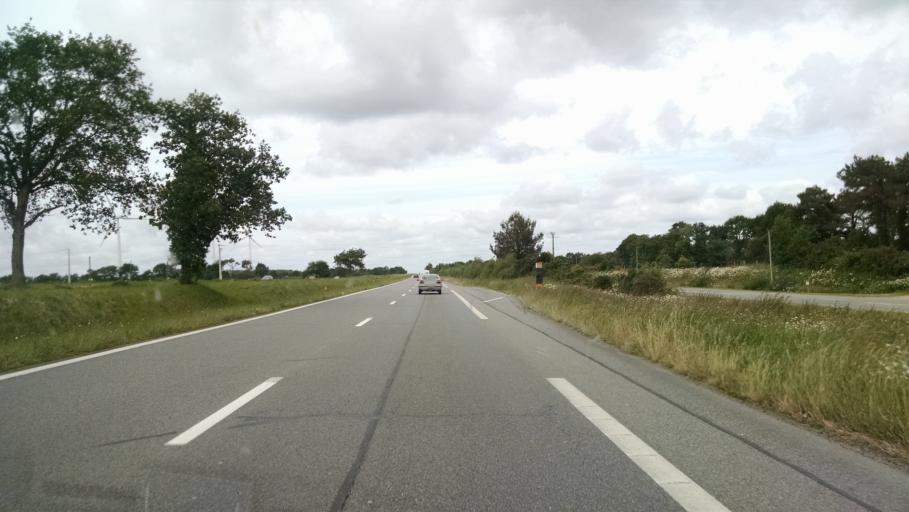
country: FR
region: Brittany
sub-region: Departement du Morbihan
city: Ambon
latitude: 47.5786
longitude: -2.5290
